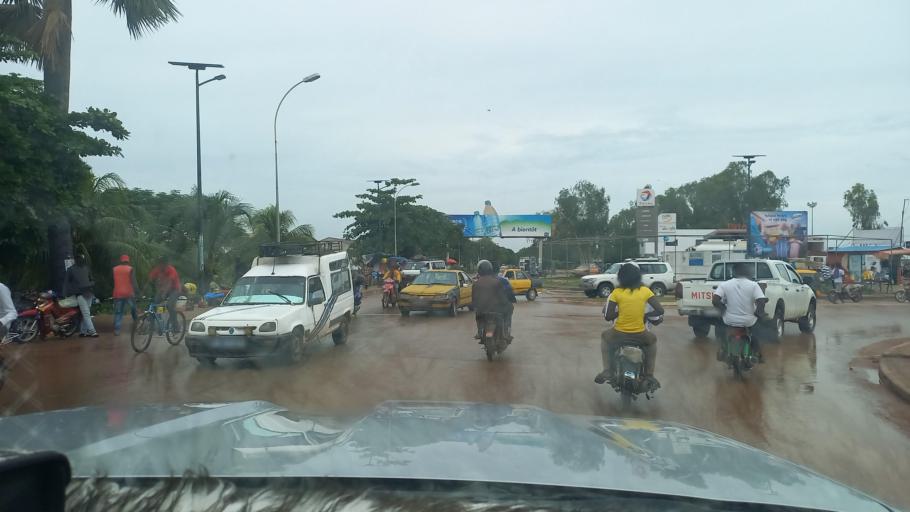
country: SN
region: Ziguinchor
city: Ziguinchor
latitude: 12.5820
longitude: -16.2640
